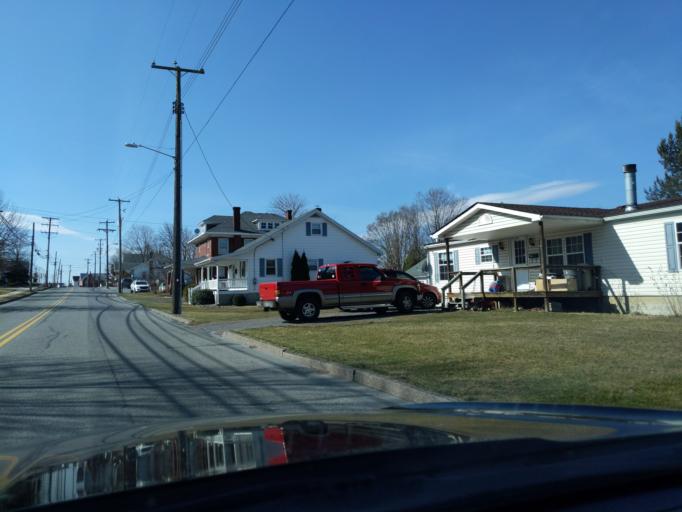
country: US
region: Pennsylvania
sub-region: Blair County
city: Martinsburg
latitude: 40.3063
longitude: -78.3278
